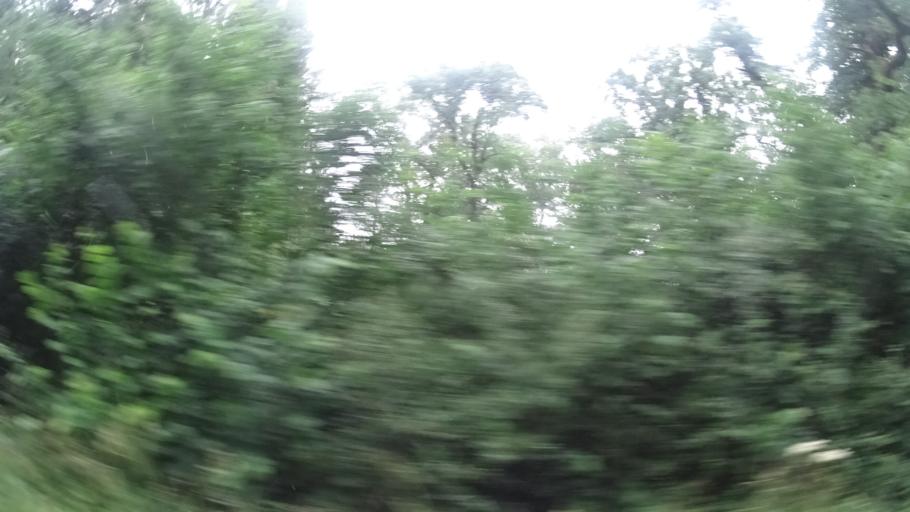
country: BE
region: Wallonia
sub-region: Province du Luxembourg
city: Saint-Leger
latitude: 49.6441
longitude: 5.6812
